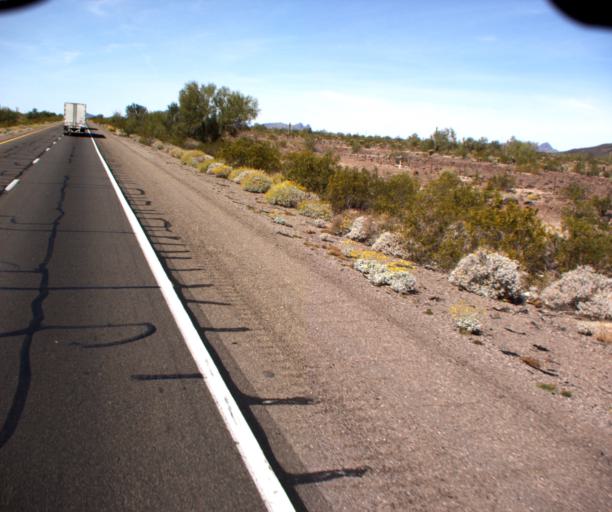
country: US
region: Arizona
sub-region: La Paz County
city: Quartzsite
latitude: 33.6505
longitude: -113.9147
